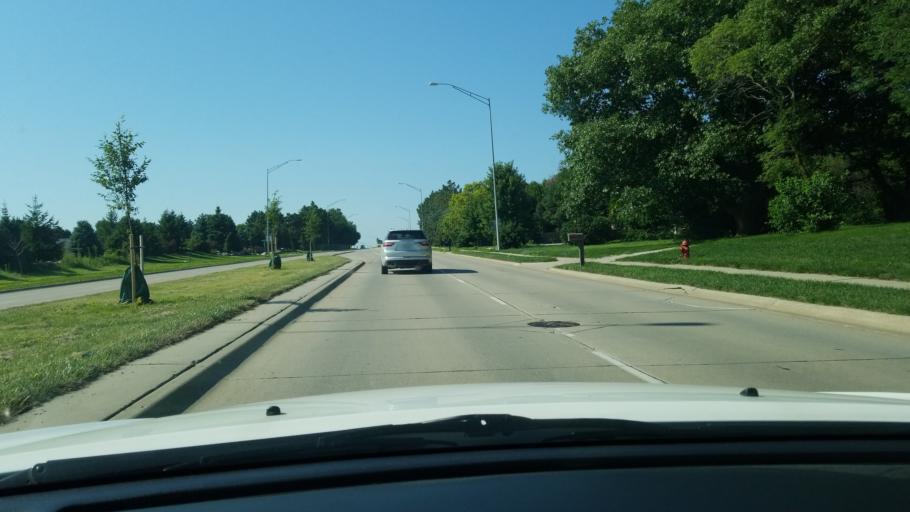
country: US
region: Nebraska
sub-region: Lancaster County
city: Lincoln
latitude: 40.7486
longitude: -96.6062
